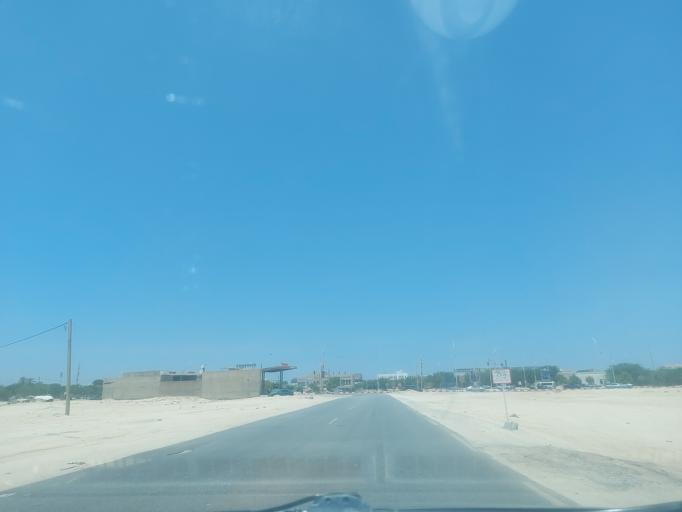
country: MR
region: Nouakchott
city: Nouakchott
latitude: 18.0882
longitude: -15.9592
